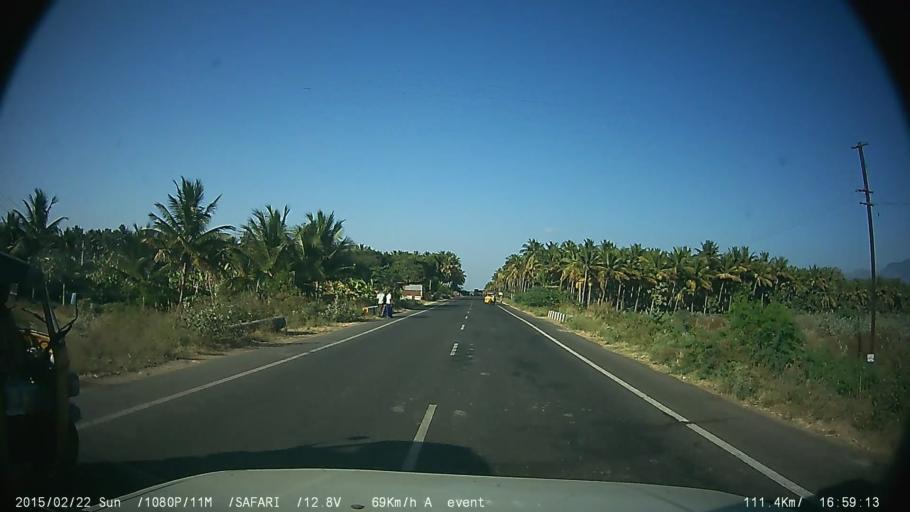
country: IN
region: Tamil Nadu
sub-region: Theni
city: Gudalur
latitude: 9.6925
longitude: 77.2547
